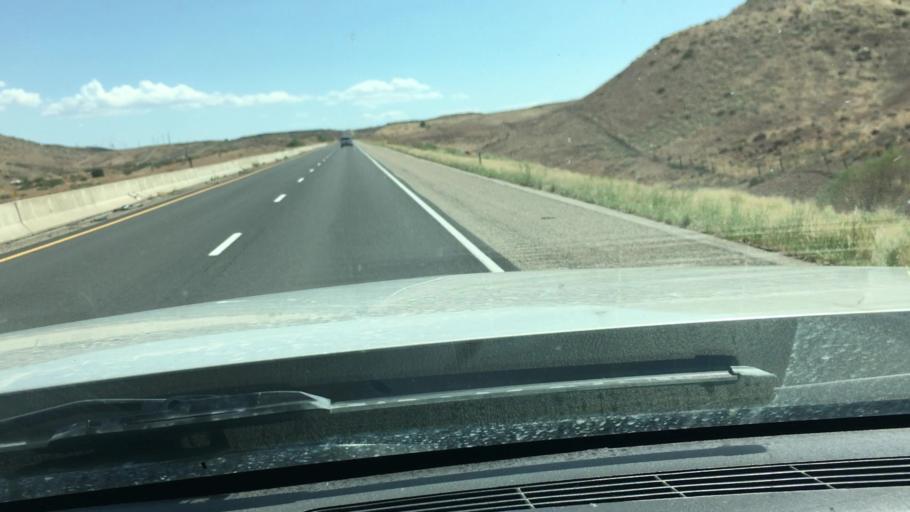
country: US
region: Utah
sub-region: Washington County
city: Hurricane
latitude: 37.2050
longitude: -113.3979
